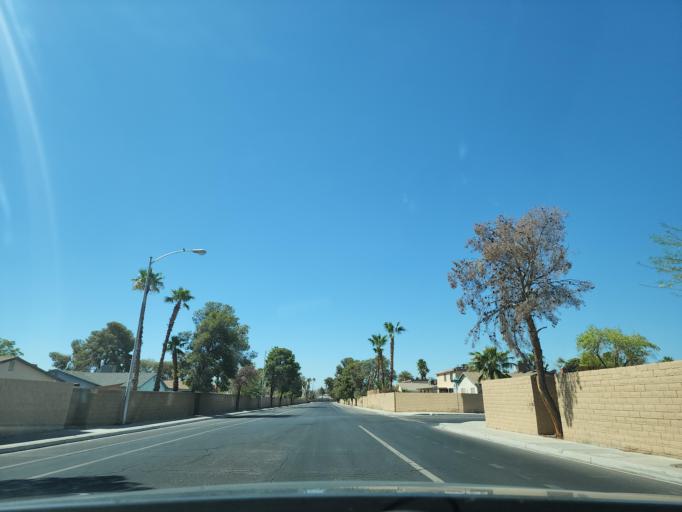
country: US
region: Nevada
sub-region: Clark County
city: Spring Valley
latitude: 36.1137
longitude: -115.2520
